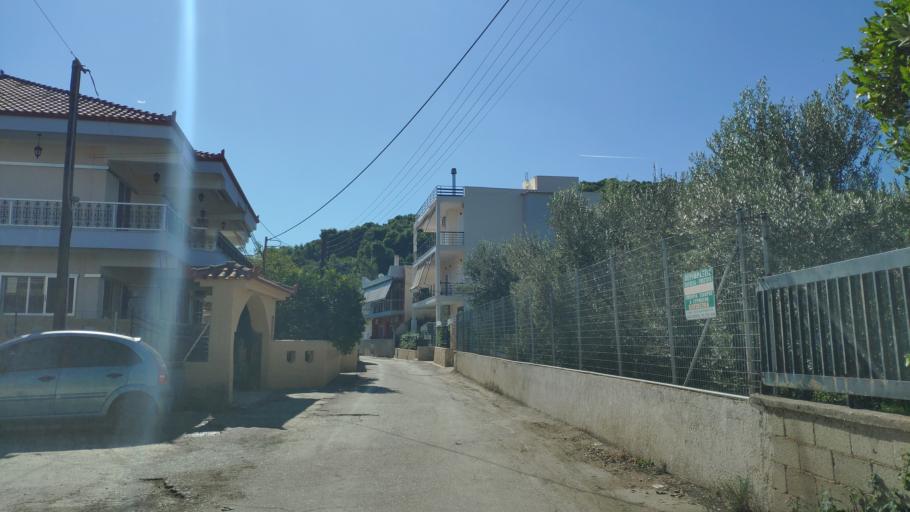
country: GR
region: Peloponnese
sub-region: Nomos Korinthias
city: Loutra Oraias Elenis
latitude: 37.8479
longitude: 22.9996
